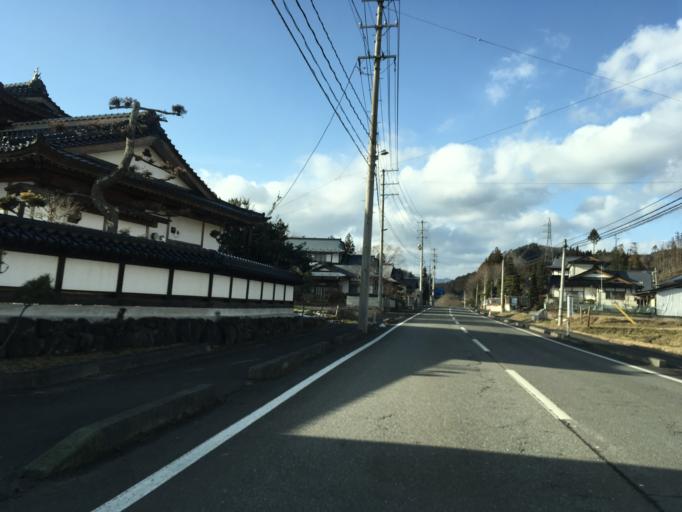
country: JP
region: Miyagi
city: Furukawa
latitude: 38.7963
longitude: 140.8405
